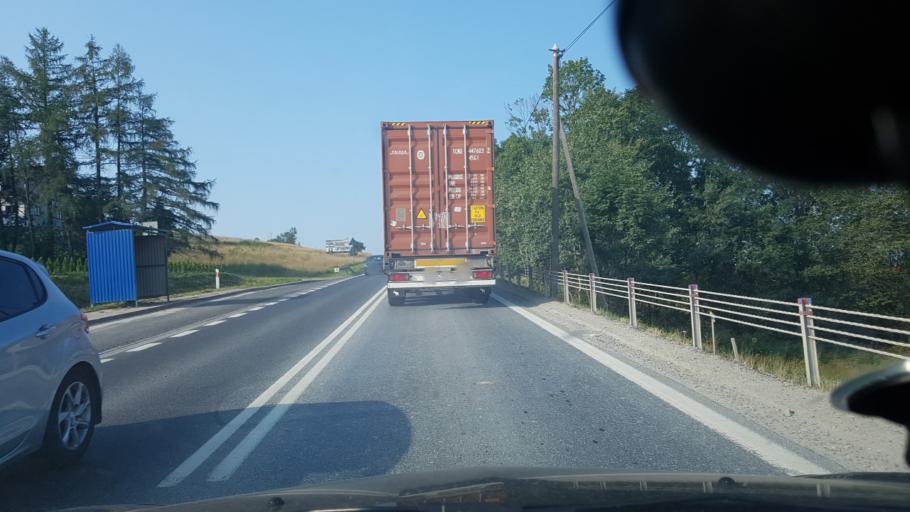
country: PL
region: Lesser Poland Voivodeship
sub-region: Powiat suski
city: Naprawa
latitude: 49.6665
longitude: 19.8910
